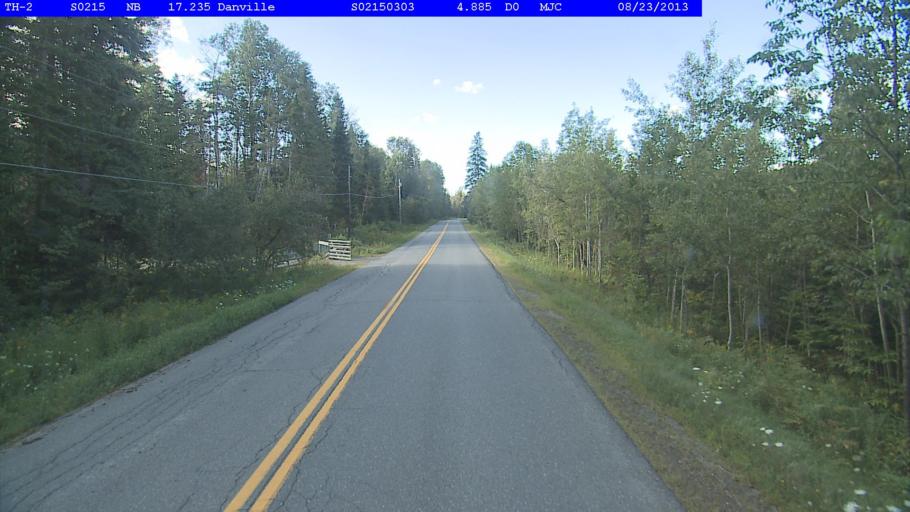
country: US
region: Vermont
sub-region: Caledonia County
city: St Johnsbury
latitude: 44.4342
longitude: -72.1419
